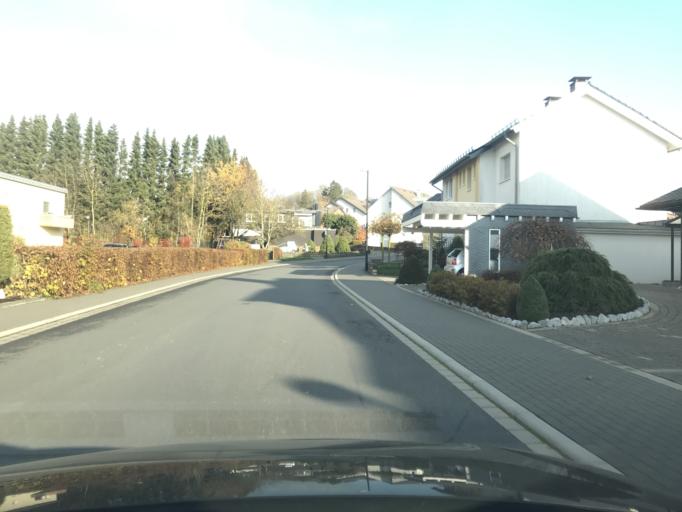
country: DE
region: North Rhine-Westphalia
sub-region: Regierungsbezirk Arnsberg
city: Brilon
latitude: 51.3915
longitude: 8.5590
